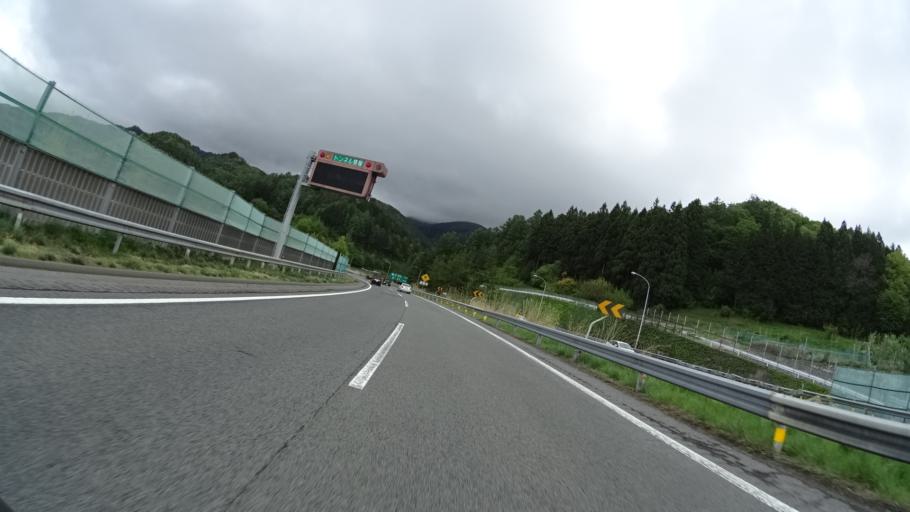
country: JP
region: Nagano
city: Nagano-shi
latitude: 36.5175
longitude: 138.0721
